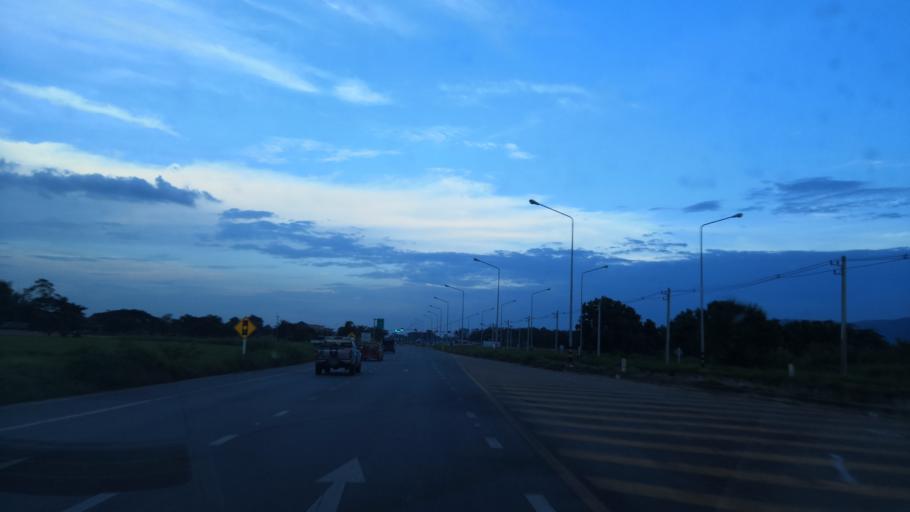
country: TH
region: Chiang Rai
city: Chiang Rai
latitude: 19.8487
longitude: 99.8112
